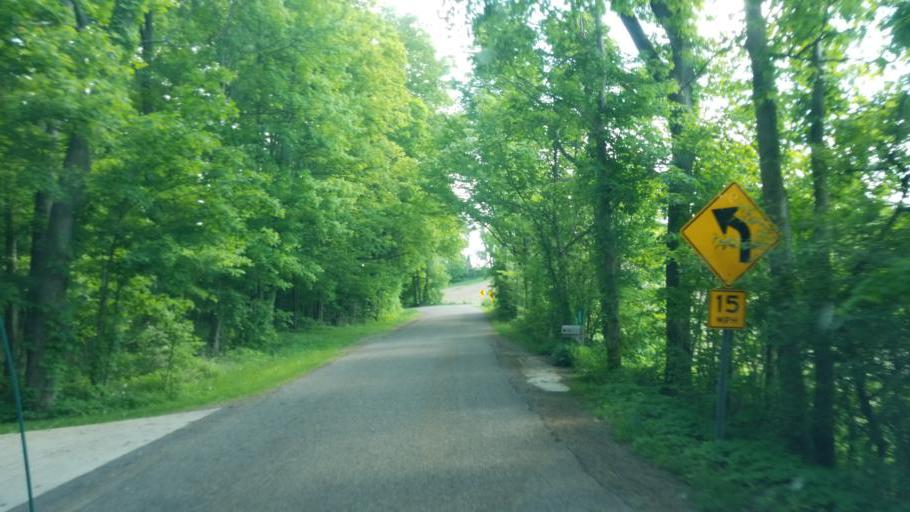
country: US
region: Ohio
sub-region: Sandusky County
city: Bellville
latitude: 40.6469
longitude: -82.5256
